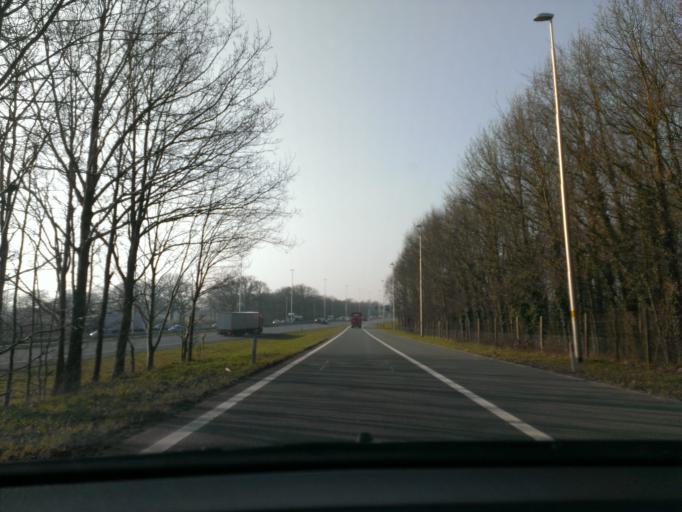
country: NL
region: Overijssel
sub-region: Gemeente Borne
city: Borne
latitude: 52.2950
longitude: 6.7273
